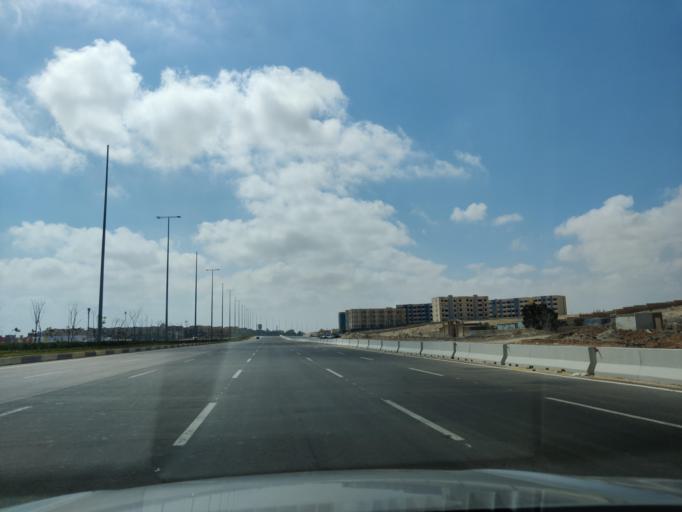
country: EG
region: Muhafazat Matruh
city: Al `Alamayn
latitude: 30.9592
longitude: 28.7605
